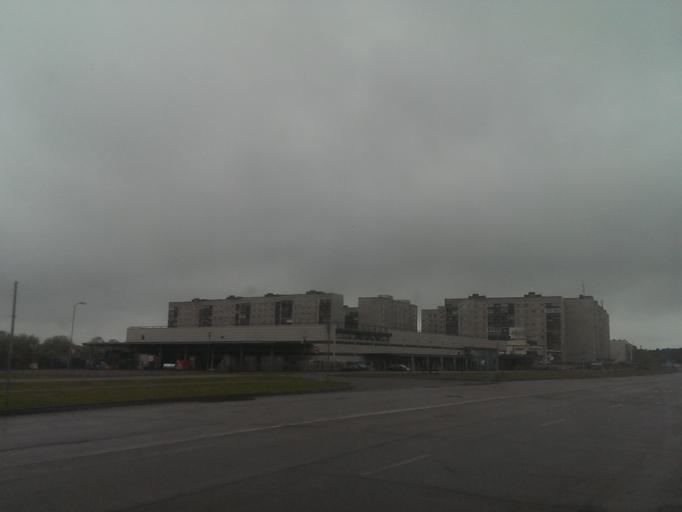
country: LV
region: Ventspils
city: Ventspils
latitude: 57.4055
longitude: 21.6065
